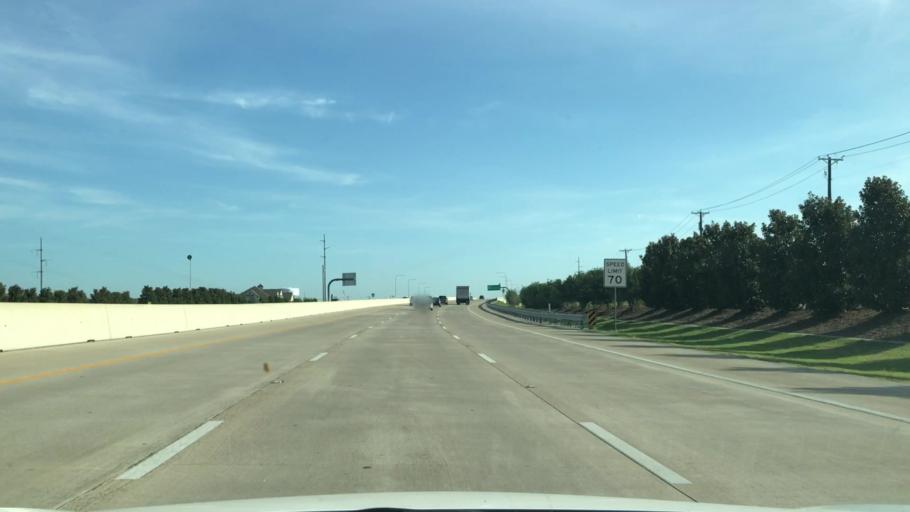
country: US
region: Texas
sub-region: Dallas County
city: Rowlett
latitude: 32.8868
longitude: -96.5565
